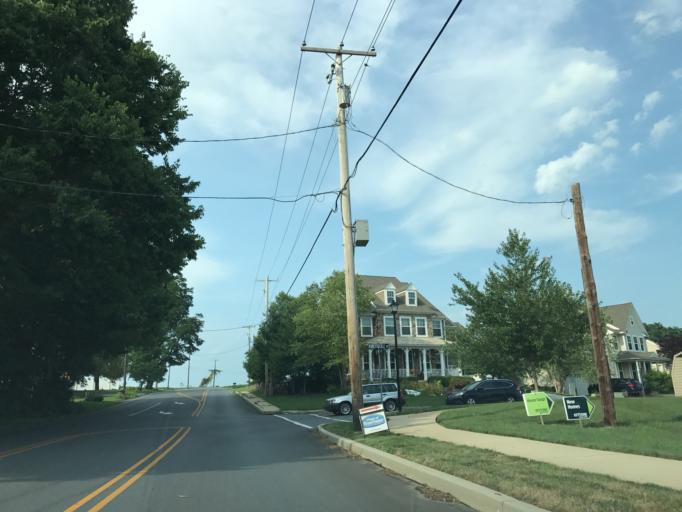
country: US
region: Pennsylvania
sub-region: Lancaster County
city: Marietta
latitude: 40.0665
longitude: -76.5395
